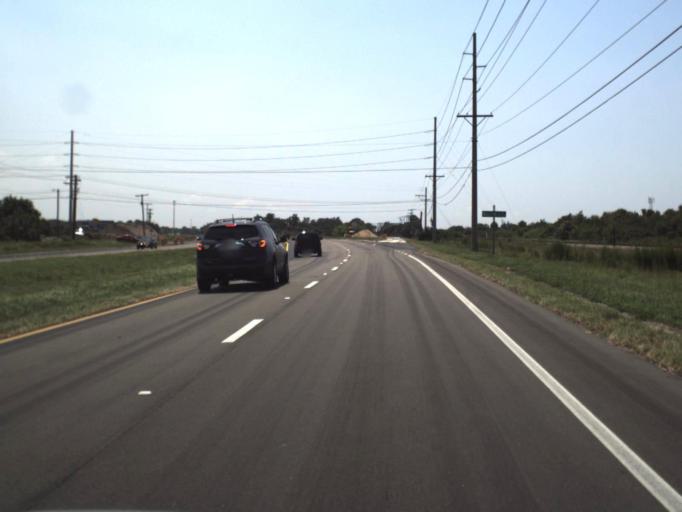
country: US
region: Florida
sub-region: Hillsborough County
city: Ruskin
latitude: 27.6853
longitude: -82.4724
